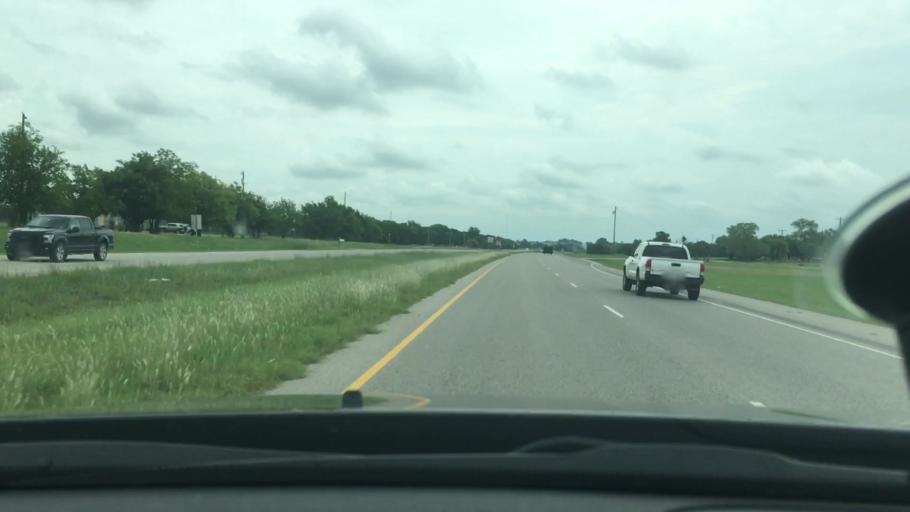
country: US
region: Oklahoma
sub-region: Carter County
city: Wilson
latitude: 34.1735
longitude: -97.4368
